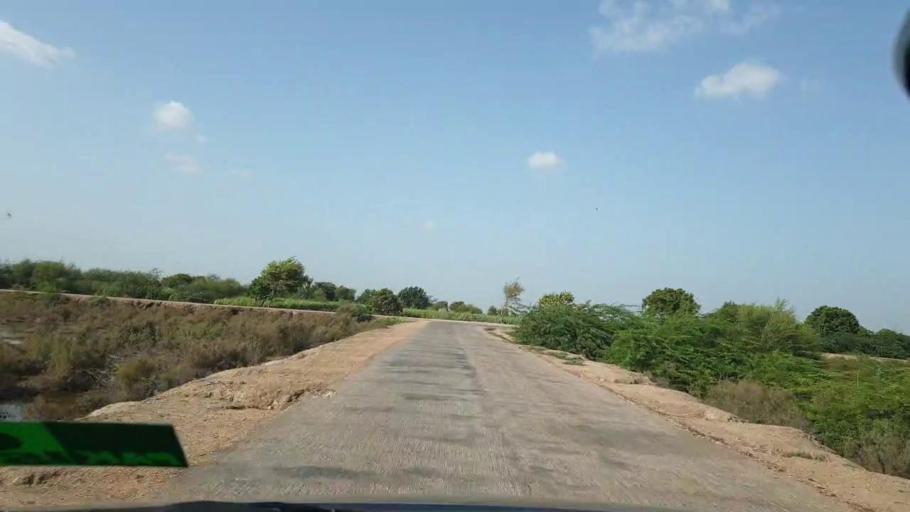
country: PK
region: Sindh
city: Tando Bago
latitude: 24.7194
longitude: 69.1940
